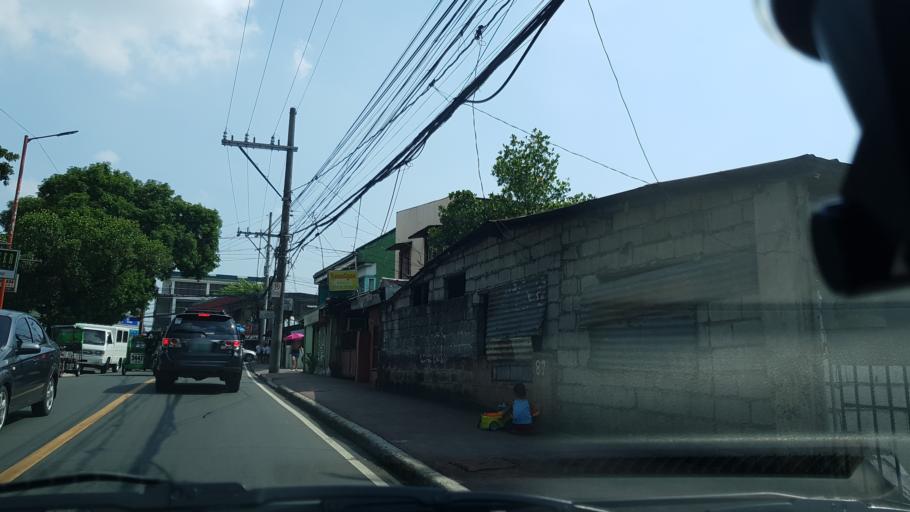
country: PH
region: Calabarzon
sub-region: Province of Rizal
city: Antipolo
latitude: 14.6621
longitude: 121.1123
